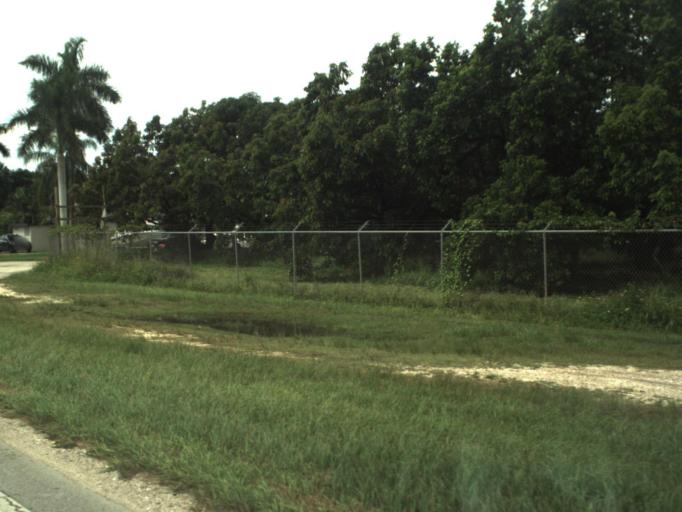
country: US
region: Florida
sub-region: Miami-Dade County
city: Naranja
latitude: 25.5338
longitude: -80.4780
